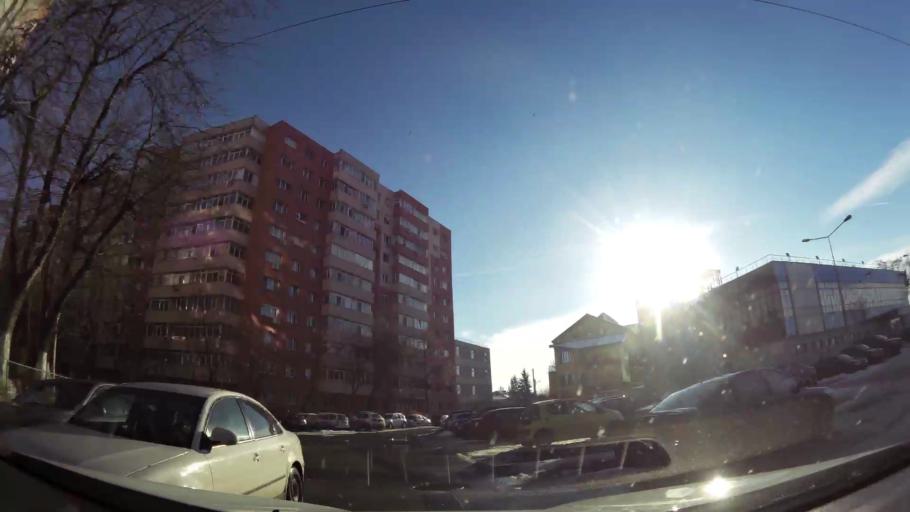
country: RO
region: Bucuresti
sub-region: Municipiul Bucuresti
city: Bucuresti
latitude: 44.3941
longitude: 26.0912
